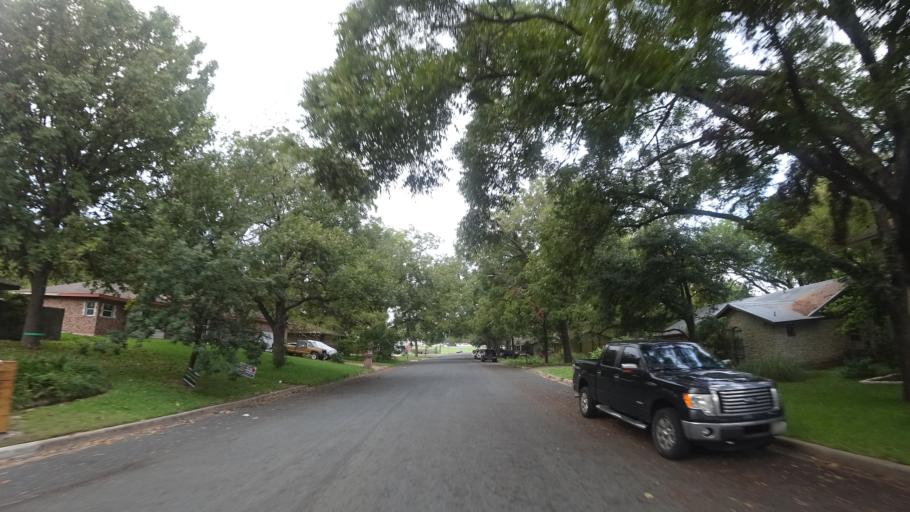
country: US
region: Texas
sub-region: Travis County
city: Austin
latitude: 30.3488
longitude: -97.6912
